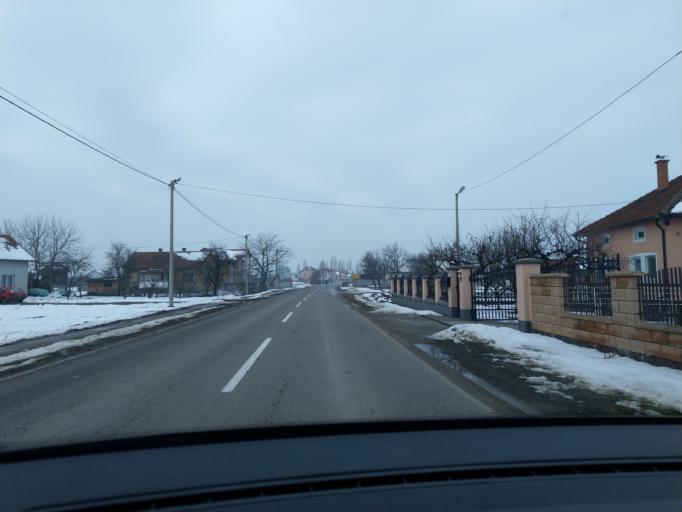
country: BA
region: Republika Srpska
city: Velika Obarska
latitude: 44.7965
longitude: 19.1748
